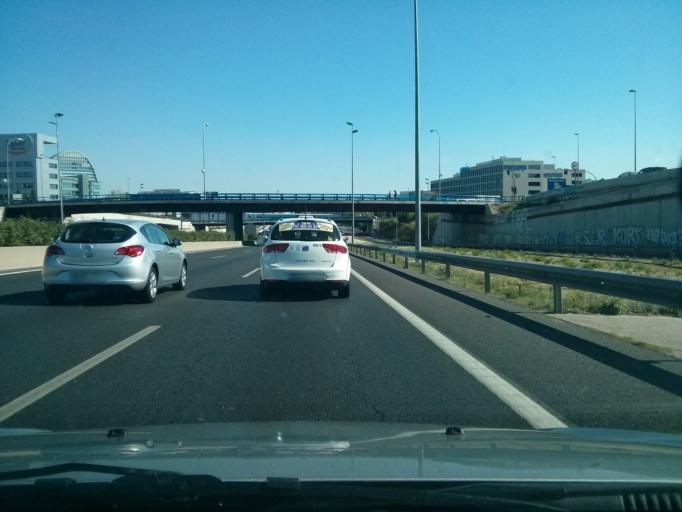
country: ES
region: Madrid
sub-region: Provincia de Madrid
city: Las Tablas
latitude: 40.4938
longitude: -3.6687
